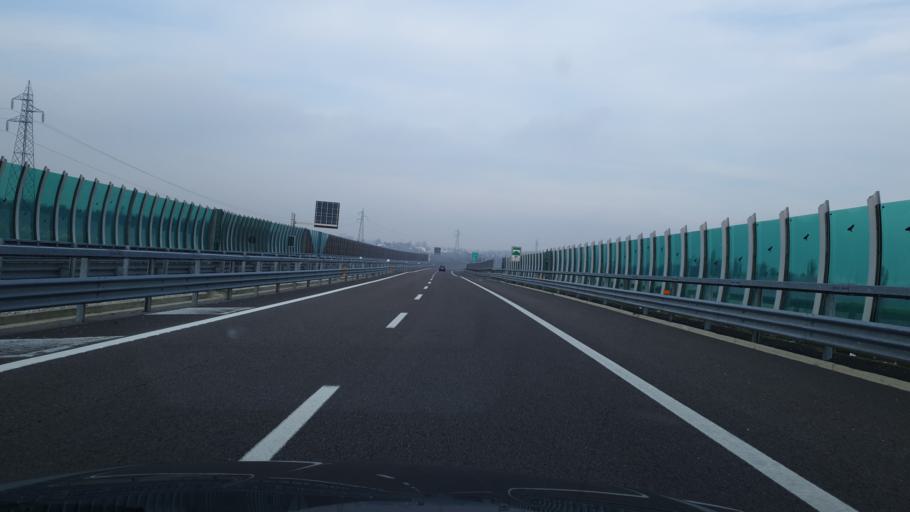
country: IT
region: Veneto
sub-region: Provincia di Padova
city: Saletto
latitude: 45.2253
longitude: 11.5514
